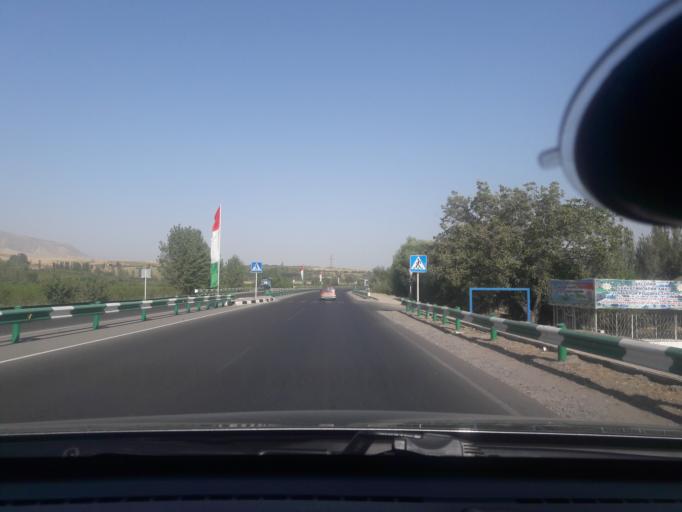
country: TJ
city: Shahrinav
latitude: 38.5753
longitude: 68.3547
